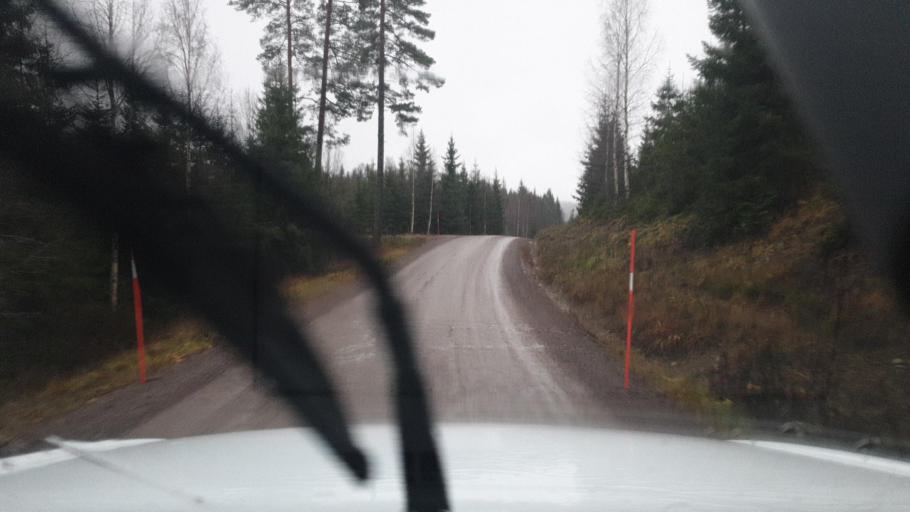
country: SE
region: Vaermland
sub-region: Arvika Kommun
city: Arvika
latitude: 59.9485
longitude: 12.6614
